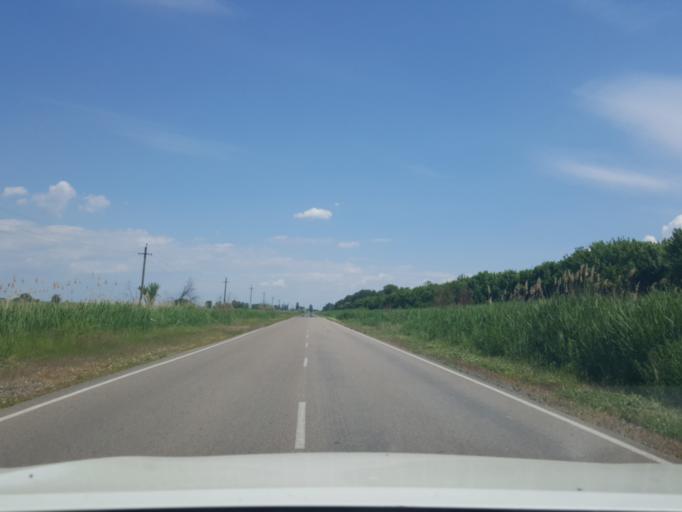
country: RO
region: Tulcea
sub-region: Oras Isaccea
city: Isaccea
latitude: 45.3061
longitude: 28.4088
